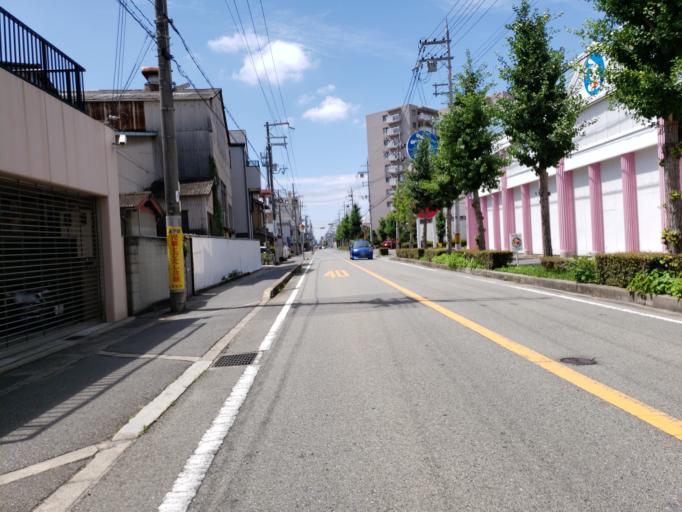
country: JP
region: Hyogo
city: Kakogawacho-honmachi
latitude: 34.7136
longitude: 134.8900
